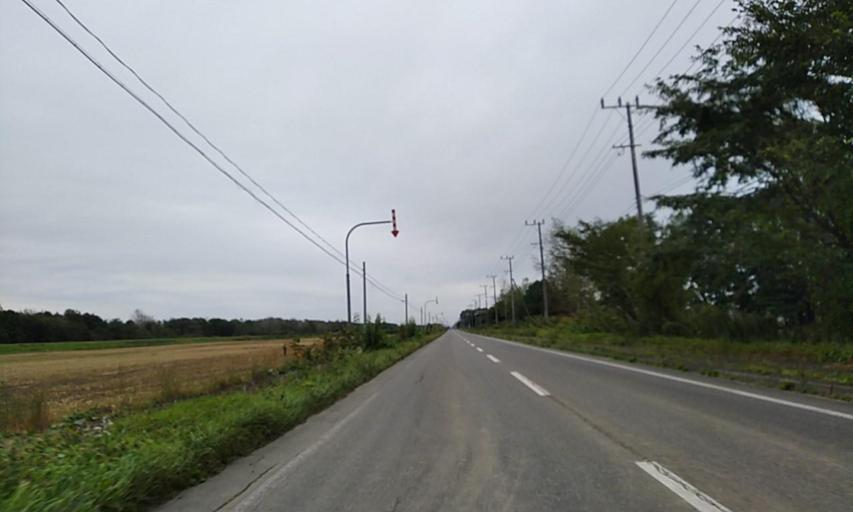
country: JP
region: Hokkaido
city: Obihiro
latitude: 42.6467
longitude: 143.0986
